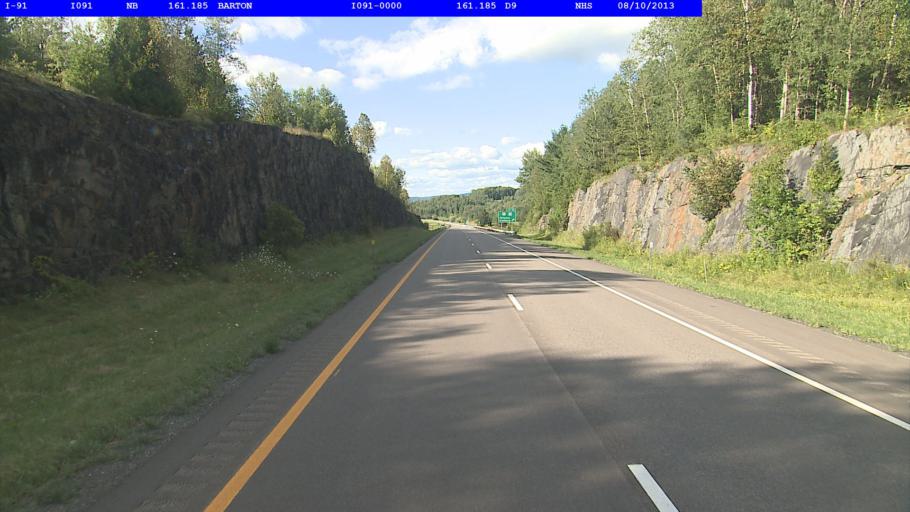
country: US
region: Vermont
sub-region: Orleans County
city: Newport
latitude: 44.8034
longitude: -72.2135
